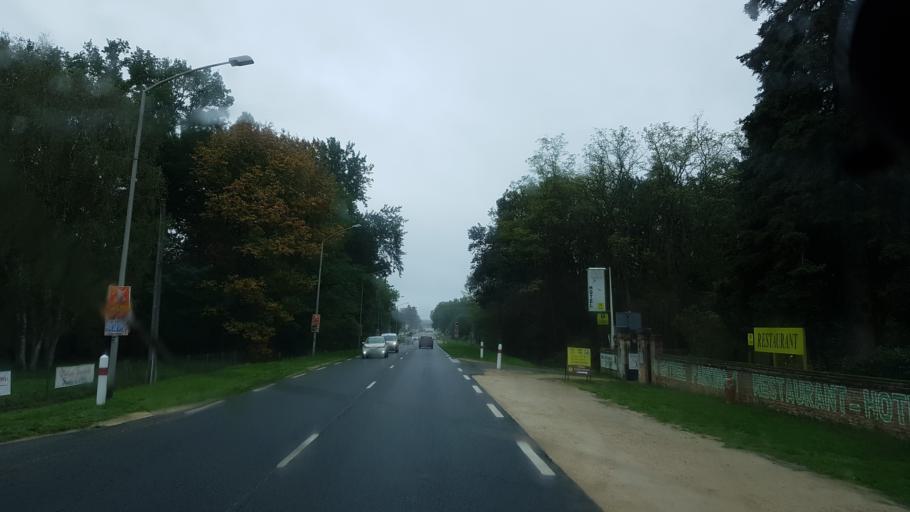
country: FR
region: Centre
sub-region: Departement du Loir-et-Cher
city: Salbris
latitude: 47.4377
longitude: 2.0481
